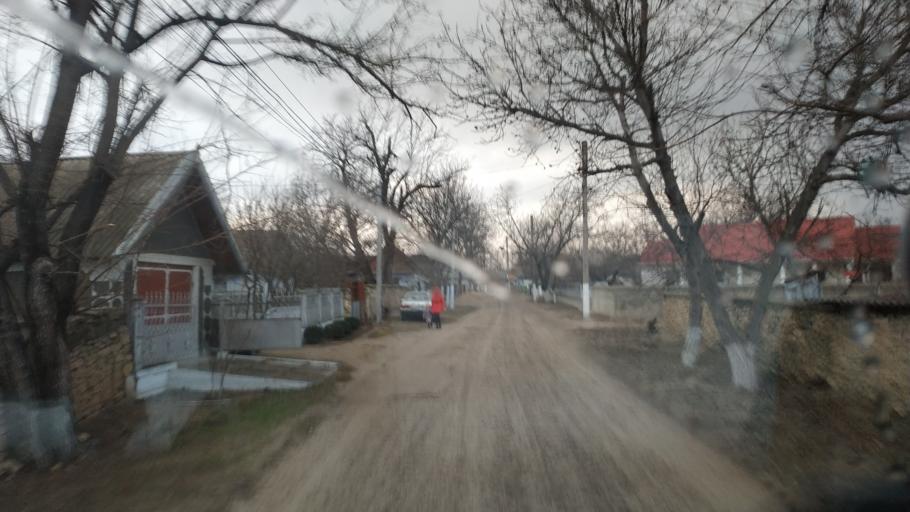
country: MD
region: Telenesti
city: Grigoriopol
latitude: 47.0918
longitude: 29.3476
